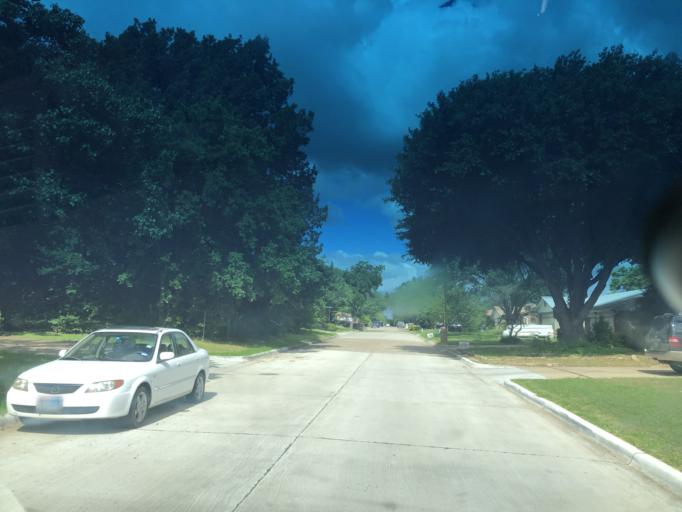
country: US
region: Texas
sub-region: Dallas County
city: Grand Prairie
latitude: 32.7094
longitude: -97.0359
